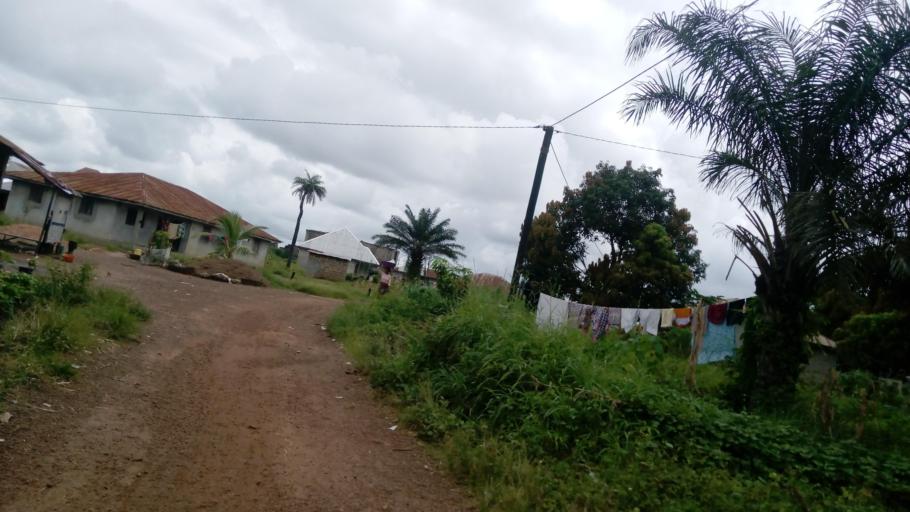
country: SL
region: Northern Province
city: Makeni
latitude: 8.9005
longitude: -12.0259
